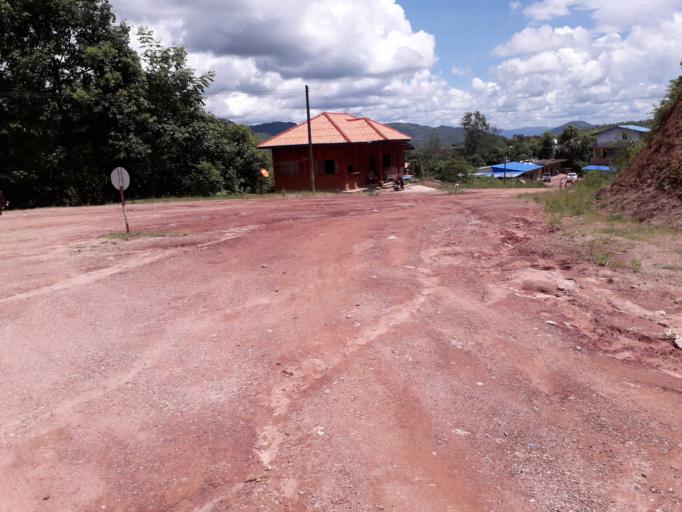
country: CN
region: Yunnan
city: Menglie
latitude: 22.2668
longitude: 101.5722
